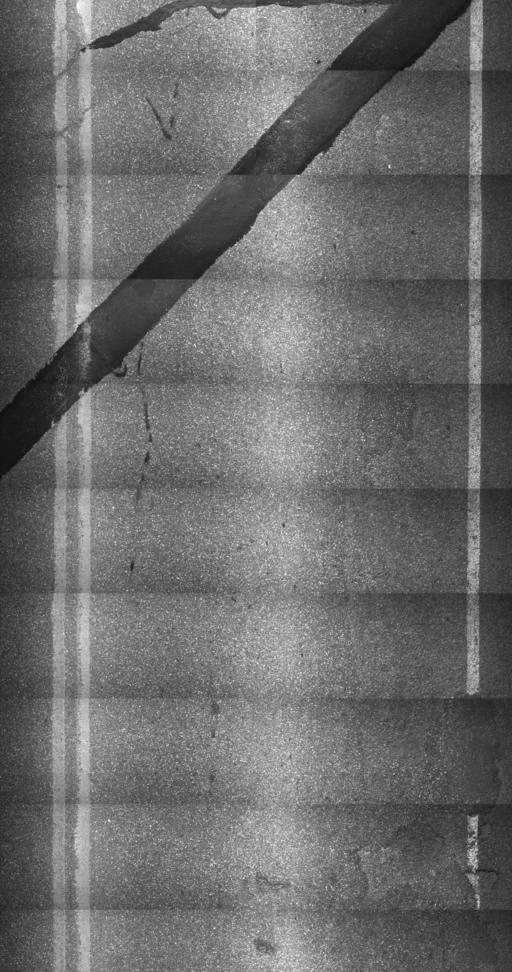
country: US
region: Vermont
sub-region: Chittenden County
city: Jericho
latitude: 44.5330
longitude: -72.9450
